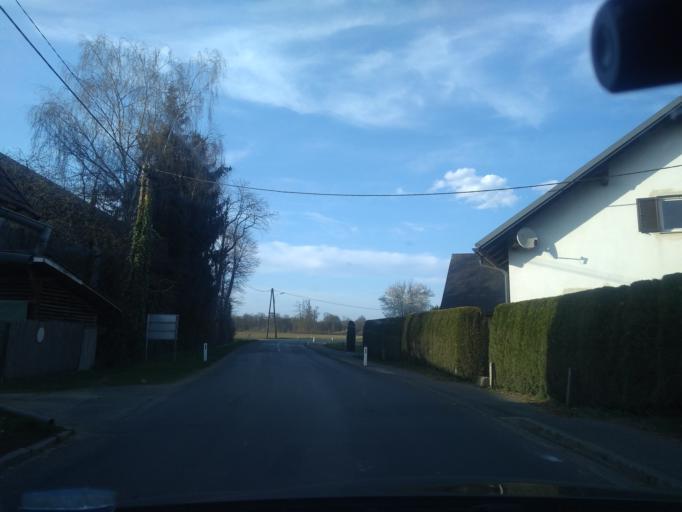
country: AT
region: Styria
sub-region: Politischer Bezirk Suedoststeiermark
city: Eichfeld
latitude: 46.7269
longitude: 15.7719
